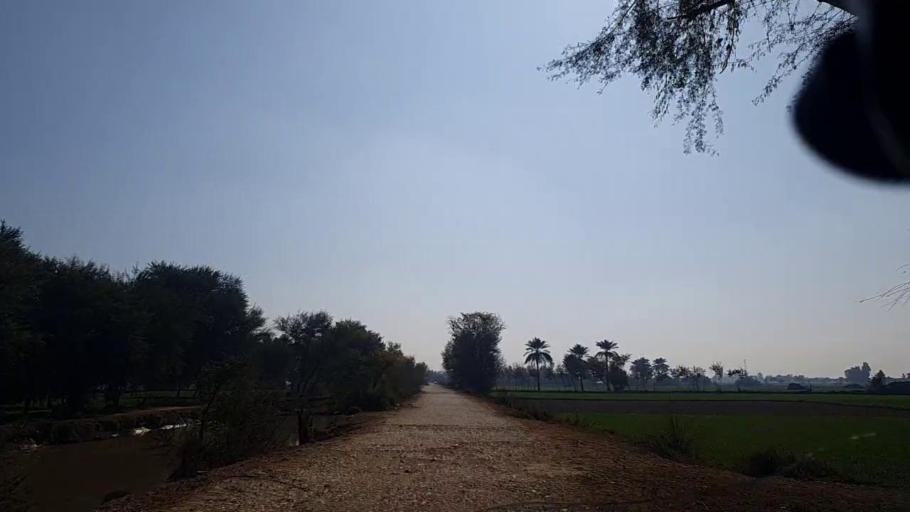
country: PK
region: Sindh
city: Khanpur
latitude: 27.7793
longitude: 69.4228
